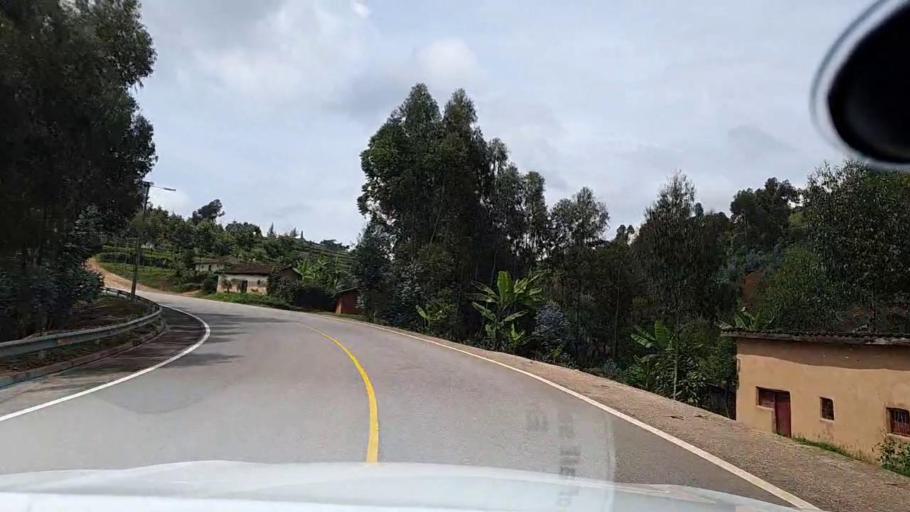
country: RW
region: Southern Province
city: Nzega
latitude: -2.5144
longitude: 29.4606
